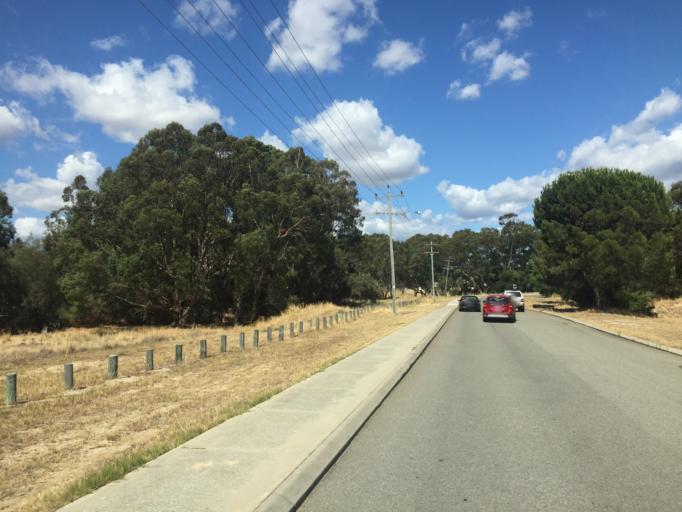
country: AU
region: Western Australia
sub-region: Belmont
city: Redcliffe
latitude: -31.9275
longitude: 115.9435
